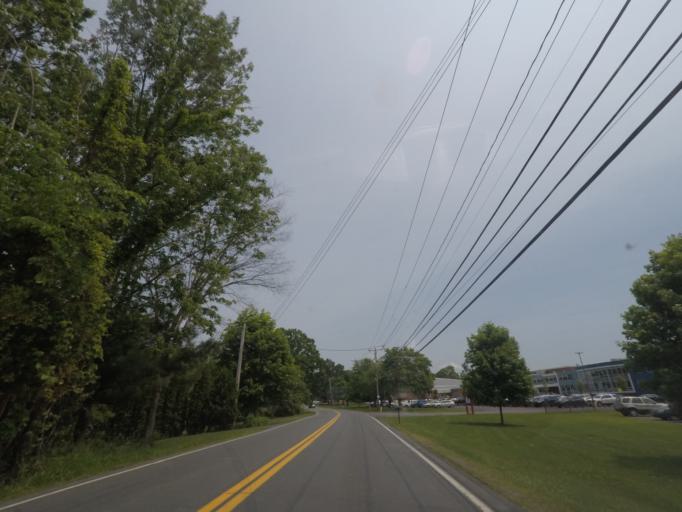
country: US
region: New York
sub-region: Rensselaer County
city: Castleton-on-Hudson
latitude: 42.5246
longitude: -73.7134
